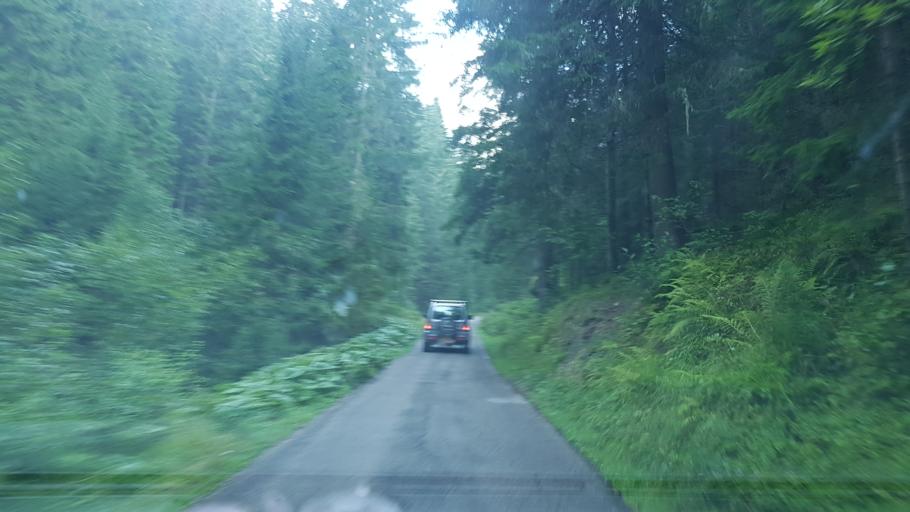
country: IT
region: Veneto
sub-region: Provincia di Belluno
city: San Pietro di Cadore
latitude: 46.5942
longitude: 12.5805
